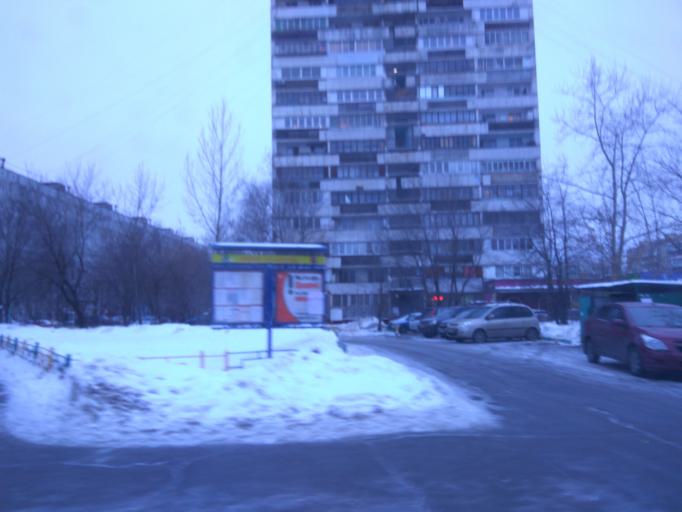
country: RU
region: Moscow
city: Gol'yanovo
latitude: 55.8171
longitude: 37.8271
